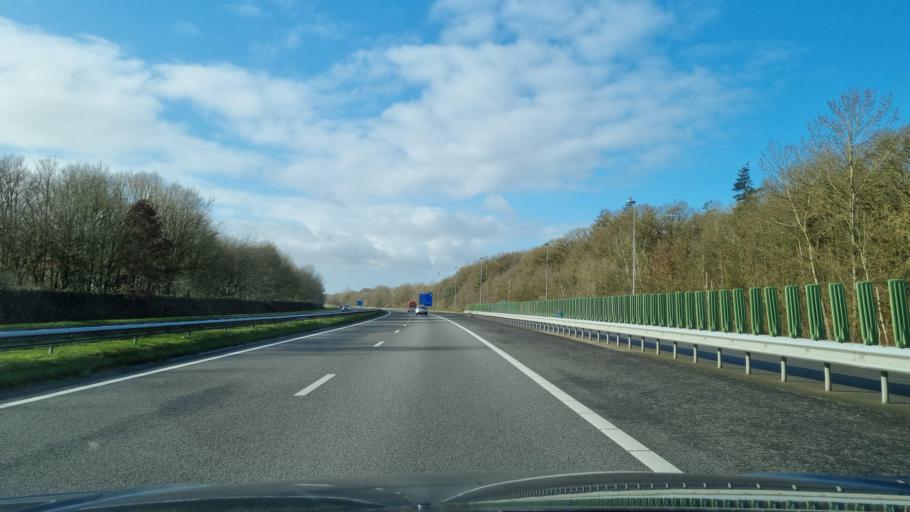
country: NL
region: Limburg
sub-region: Gemeente Gennep
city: Gennep
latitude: 51.6738
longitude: 6.0108
